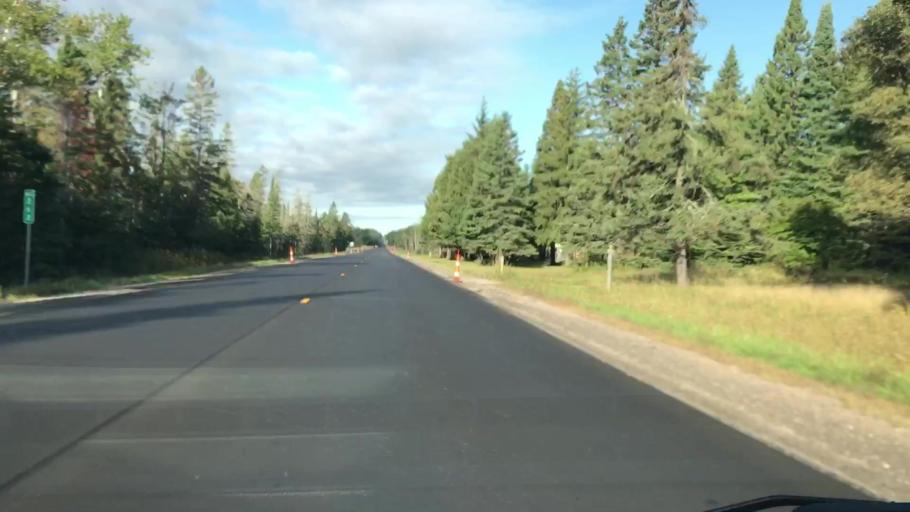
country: US
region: Michigan
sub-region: Mackinac County
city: Saint Ignace
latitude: 46.3460
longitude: -84.9435
